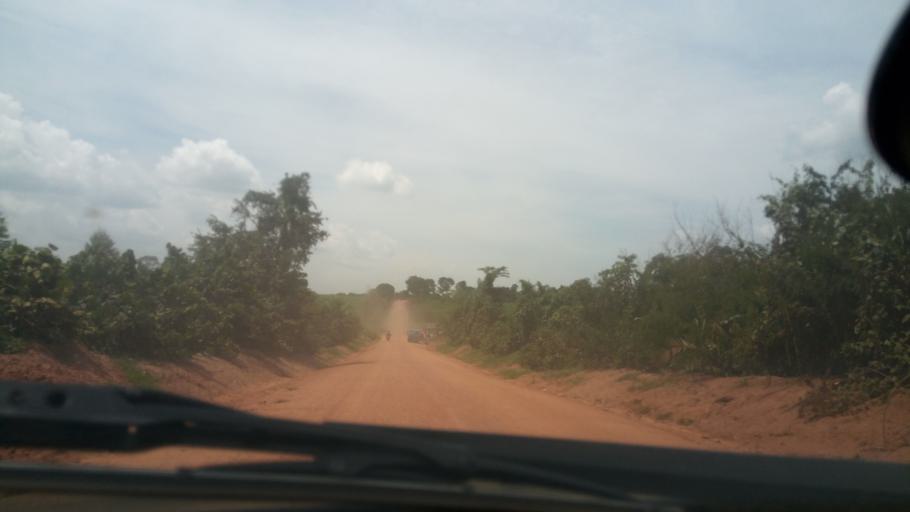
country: UG
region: Central Region
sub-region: Mityana District
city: Mityana
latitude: 0.4547
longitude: 32.0863
